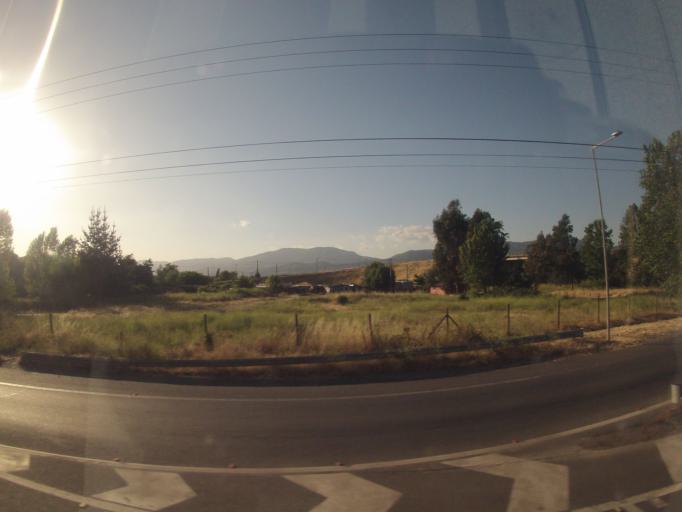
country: CL
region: O'Higgins
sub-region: Provincia de Colchagua
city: Chimbarongo
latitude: -34.6076
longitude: -70.9846
